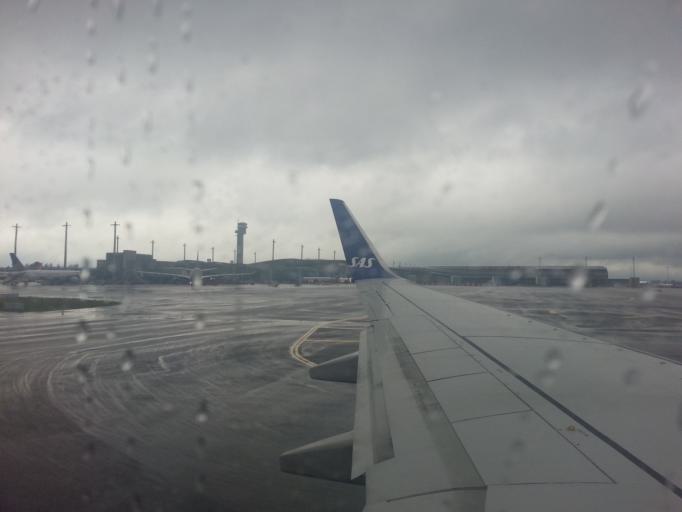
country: NO
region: Akershus
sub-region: Ullensaker
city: Jessheim
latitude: 60.1945
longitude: 11.1129
